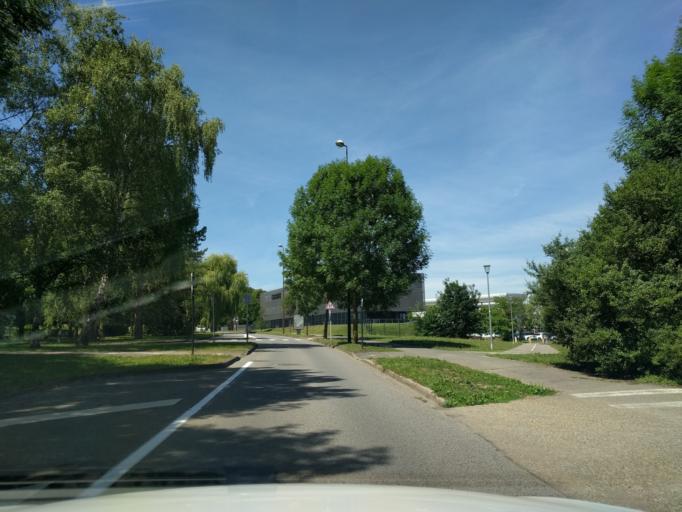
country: FR
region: Lorraine
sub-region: Departement de la Moselle
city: Saint-Julien-les-Metz
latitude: 49.1068
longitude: 6.2137
